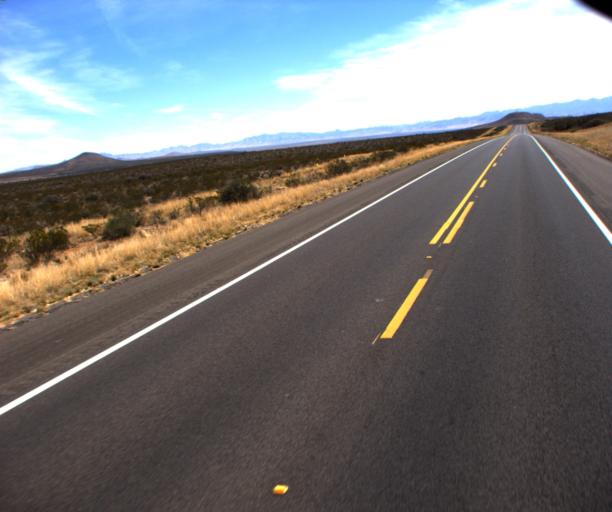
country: US
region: Arizona
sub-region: Cochise County
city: Willcox
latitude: 31.9055
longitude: -109.7520
